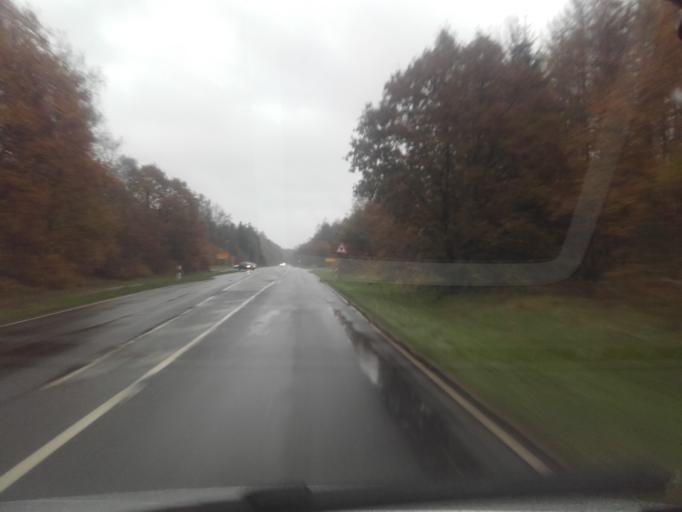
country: DE
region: Schleswig-Holstein
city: Kropp
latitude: 54.4034
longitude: 9.5097
